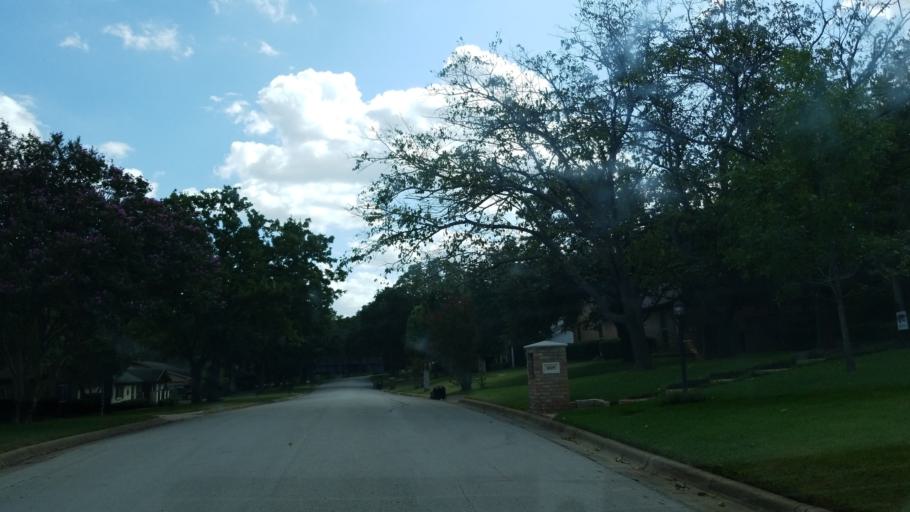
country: US
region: Texas
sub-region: Tarrant County
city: Euless
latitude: 32.8646
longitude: -97.0906
